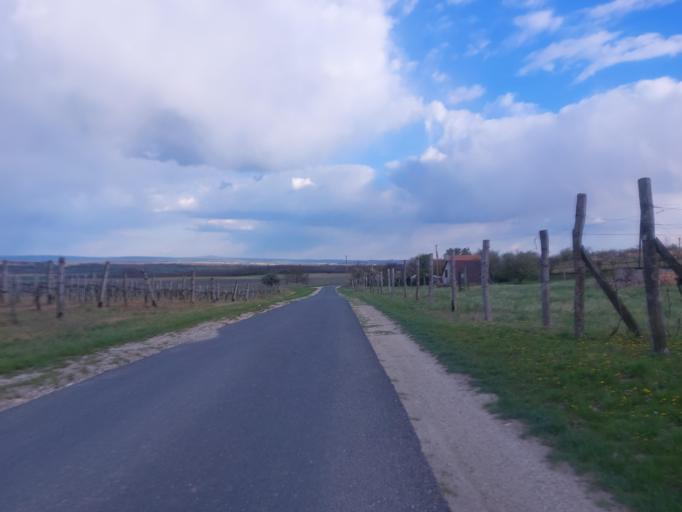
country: HU
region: Veszprem
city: Devecser
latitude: 47.1490
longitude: 17.3853
